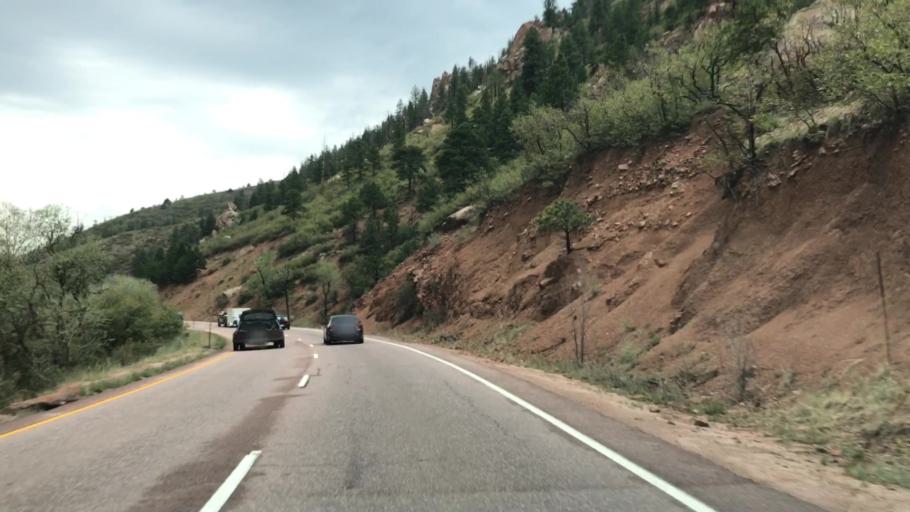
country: US
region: Colorado
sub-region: El Paso County
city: Manitou Springs
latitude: 38.8835
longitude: -104.9505
